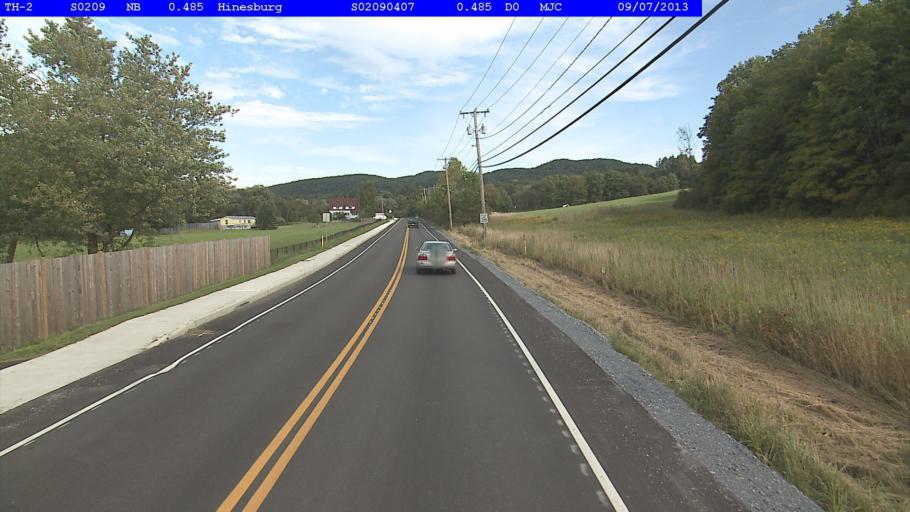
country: US
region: Vermont
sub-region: Chittenden County
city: Hinesburg
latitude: 44.3374
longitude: -73.1054
